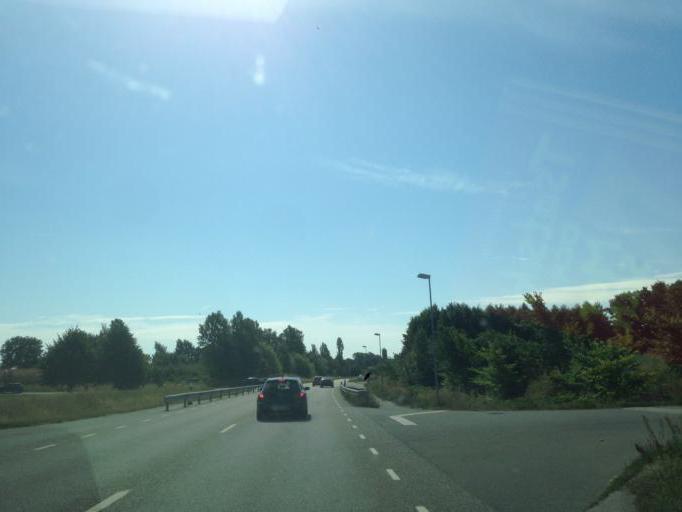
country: SE
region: Skane
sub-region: Simrishamns Kommun
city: Kivik
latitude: 55.6313
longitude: 14.2518
